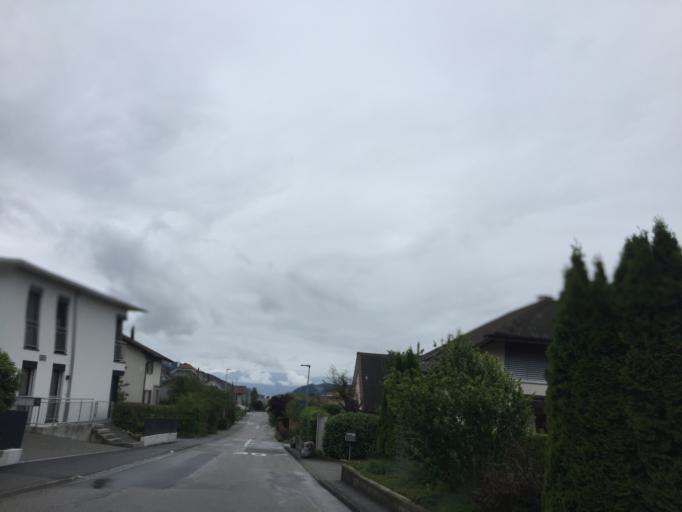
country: CH
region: Bern
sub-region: Bern-Mittelland District
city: Zaziwil
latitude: 46.9043
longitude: 7.6409
